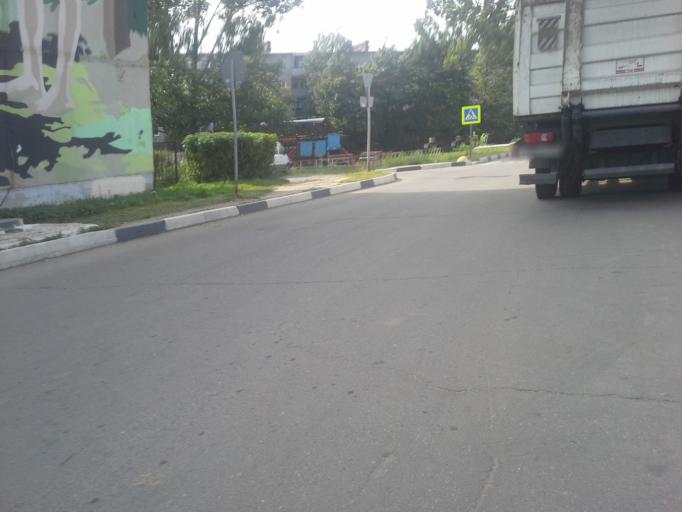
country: RU
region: Moskovskaya
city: Aprelevka
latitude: 55.5497
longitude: 37.0831
